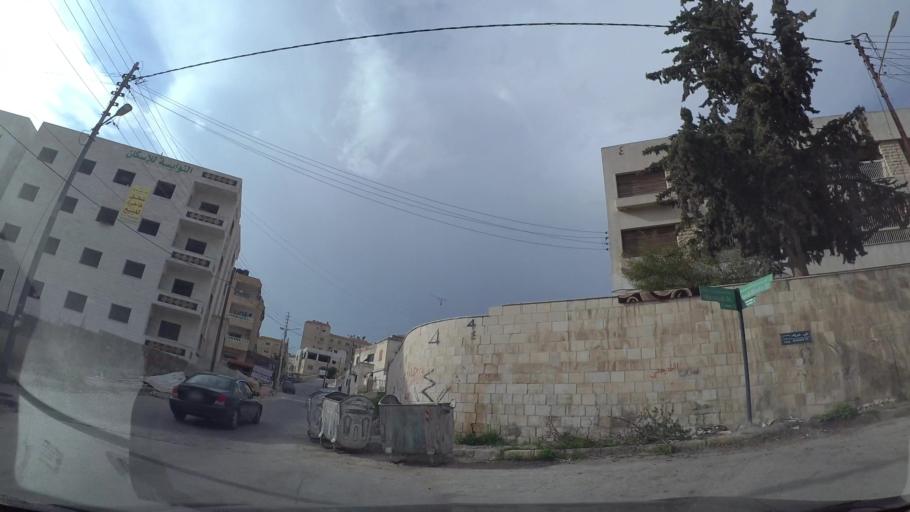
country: JO
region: Amman
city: Amman
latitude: 32.0024
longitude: 35.9477
